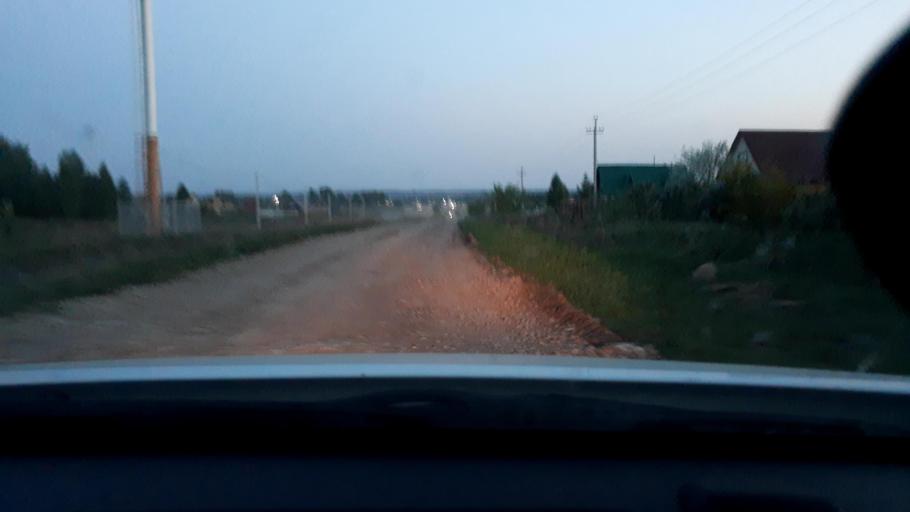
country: RU
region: Bashkortostan
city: Avdon
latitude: 54.5188
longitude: 55.8253
